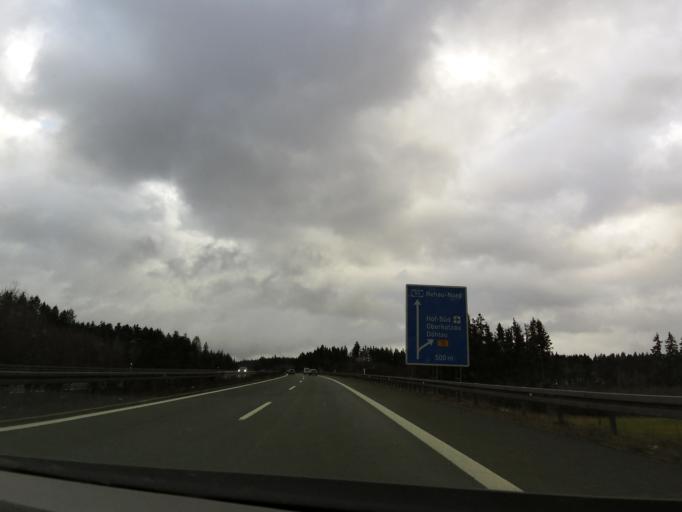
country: DE
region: Bavaria
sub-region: Upper Franconia
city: Rehau
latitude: 50.2748
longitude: 12.0245
